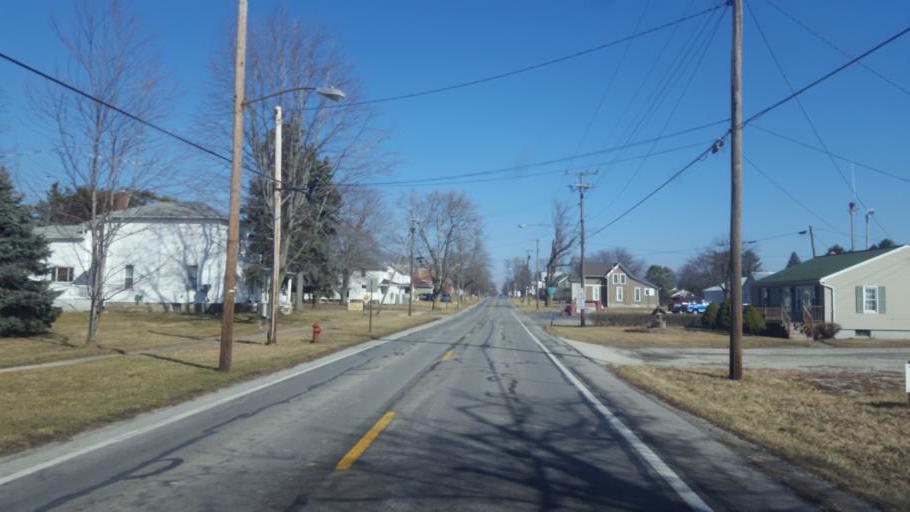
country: US
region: Ohio
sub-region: Huron County
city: Willard
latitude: 41.0601
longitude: -82.8896
